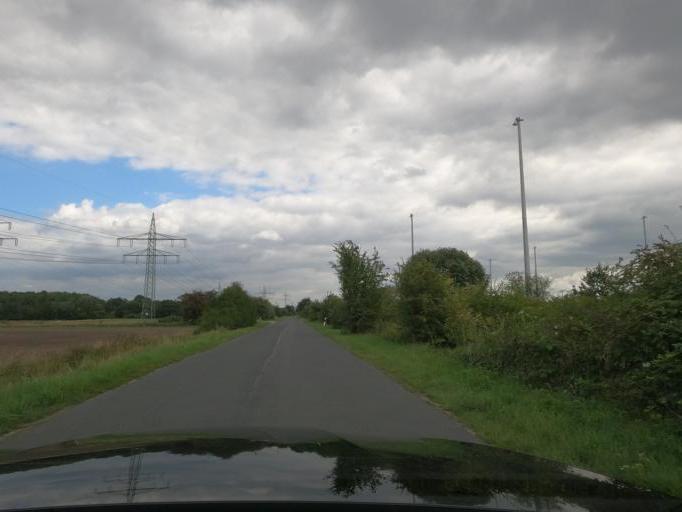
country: DE
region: Lower Saxony
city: Lehrte
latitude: 52.3796
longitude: 9.9339
